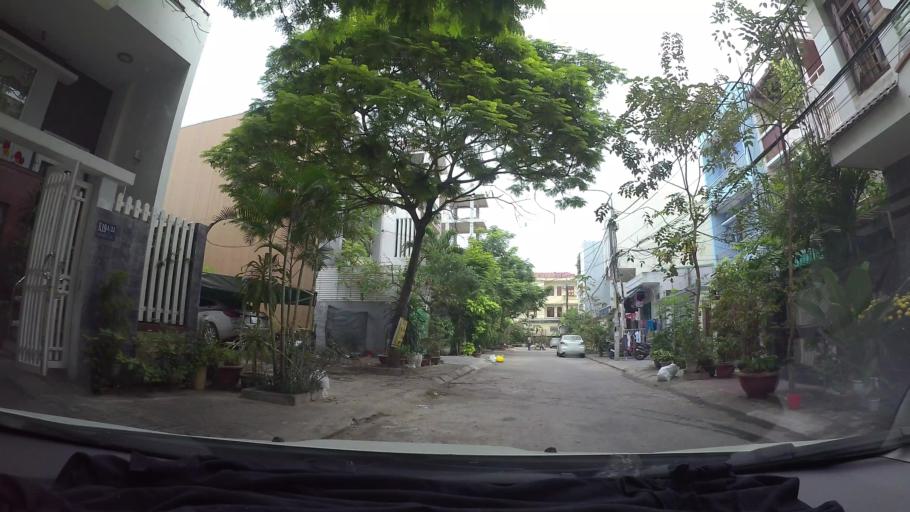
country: VN
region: Da Nang
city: Thanh Khe
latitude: 16.0701
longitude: 108.1922
